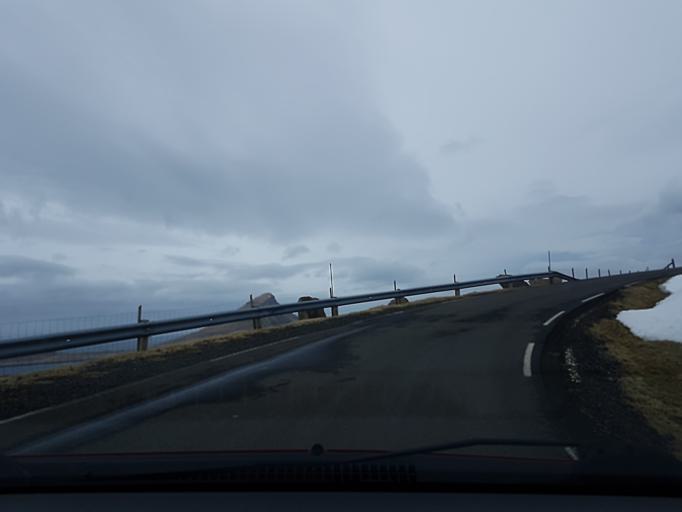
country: FO
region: Streymoy
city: Kollafjordhur
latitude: 61.9991
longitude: -6.8972
